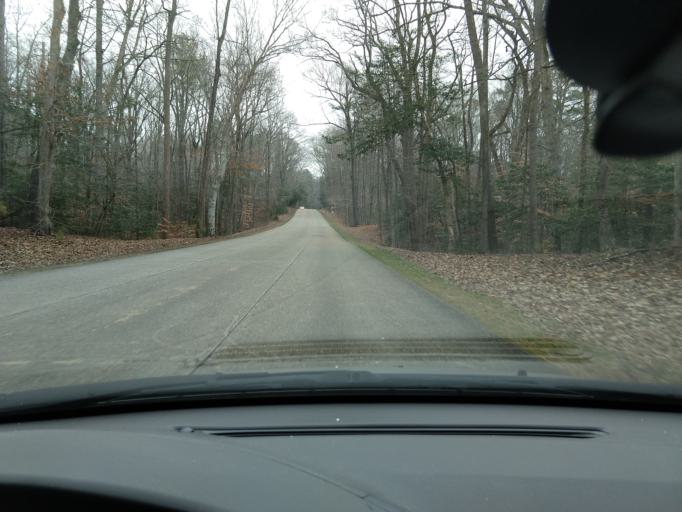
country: US
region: Virginia
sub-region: City of Williamsburg
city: Williamsburg
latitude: 37.2817
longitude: -76.6309
